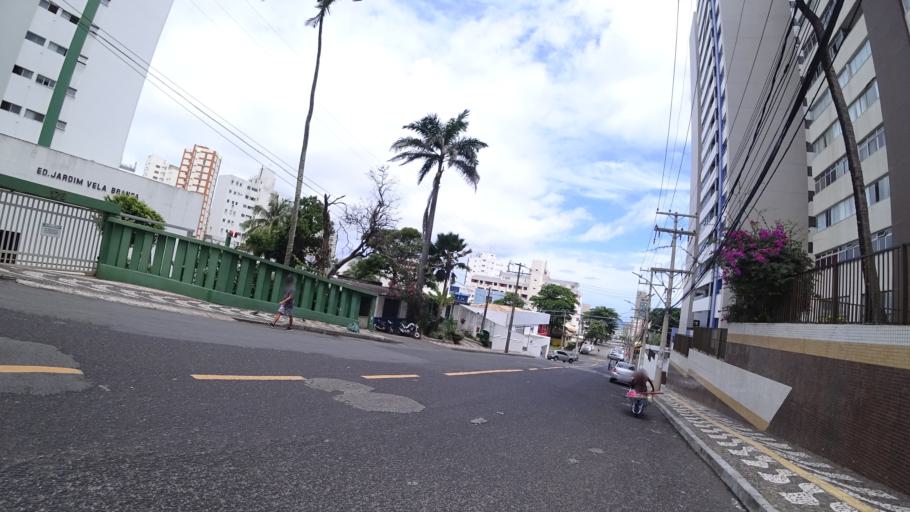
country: BR
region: Bahia
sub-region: Salvador
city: Salvador
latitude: -13.0056
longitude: -38.4633
